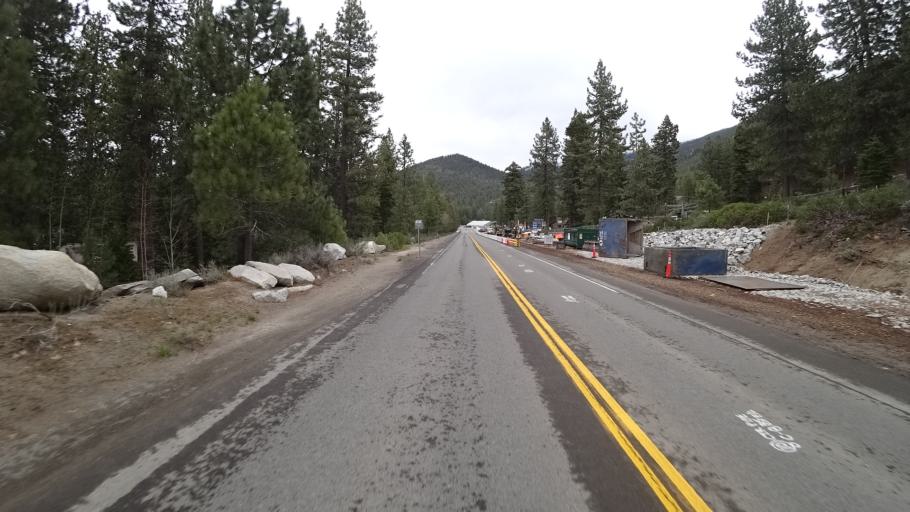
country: US
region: Nevada
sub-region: Washoe County
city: Incline Village
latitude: 39.2333
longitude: -119.9314
